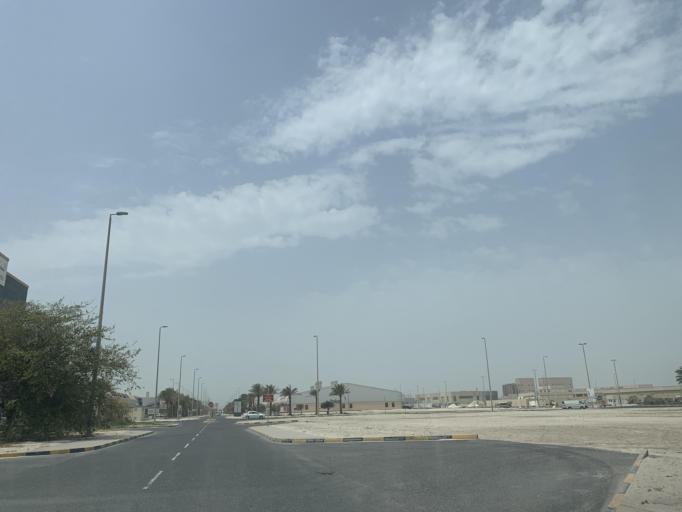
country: BH
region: Muharraq
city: Al Hadd
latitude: 26.2200
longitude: 50.6752
